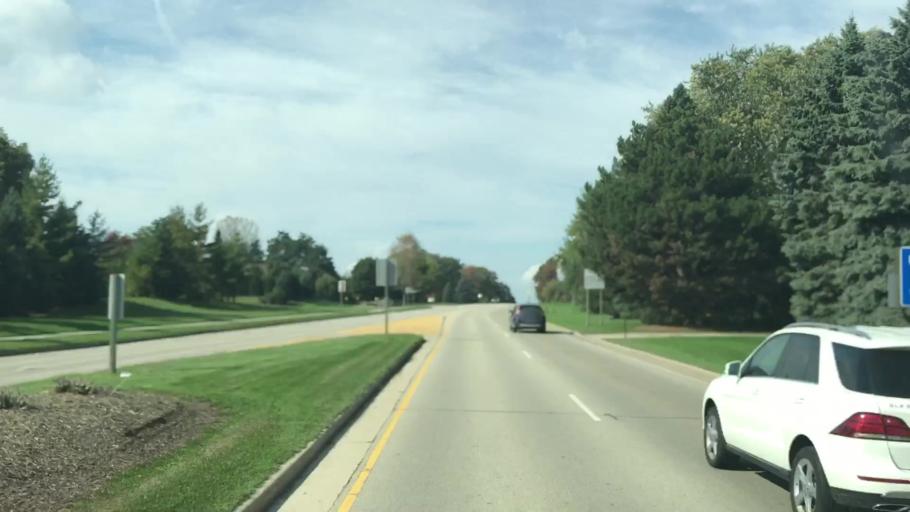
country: US
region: Wisconsin
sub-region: Ozaukee County
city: Mequon
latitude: 43.2217
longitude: -88.0066
